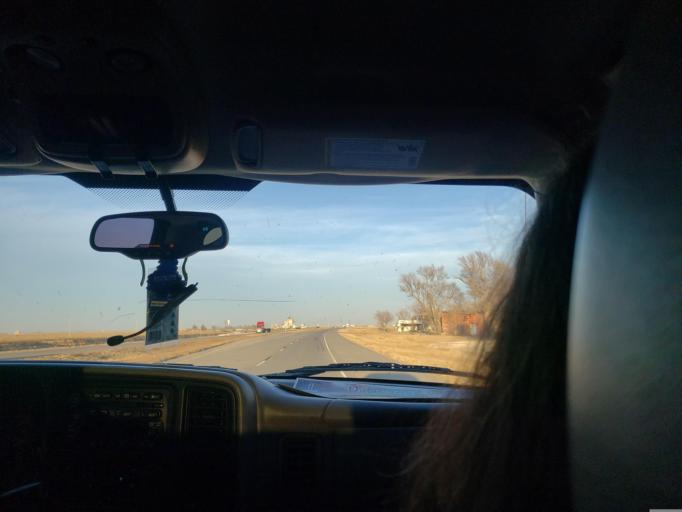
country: US
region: Oklahoma
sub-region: Texas County
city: Guymon
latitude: 36.7593
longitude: -101.3578
